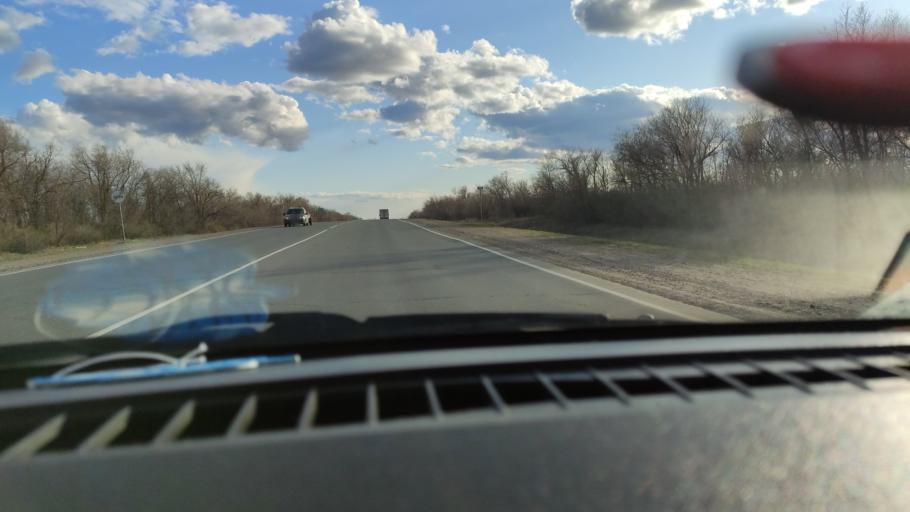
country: RU
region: Saratov
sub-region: Saratovskiy Rayon
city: Saratov
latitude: 51.7108
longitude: 46.0190
